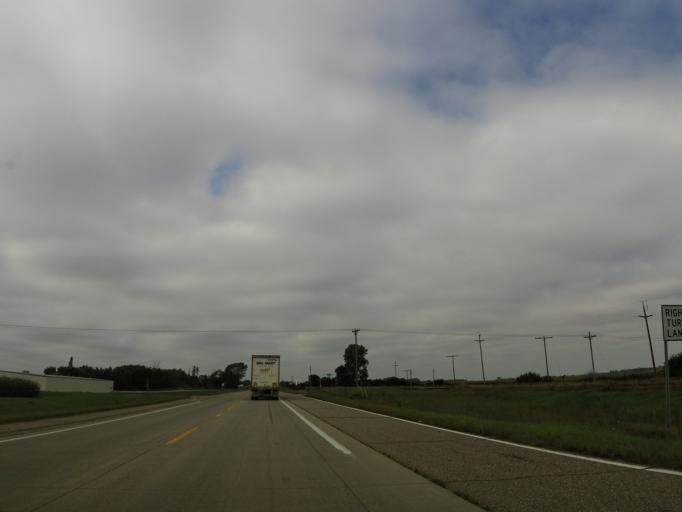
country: US
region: Minnesota
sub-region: Renville County
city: Olivia
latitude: 44.7742
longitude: -94.9548
